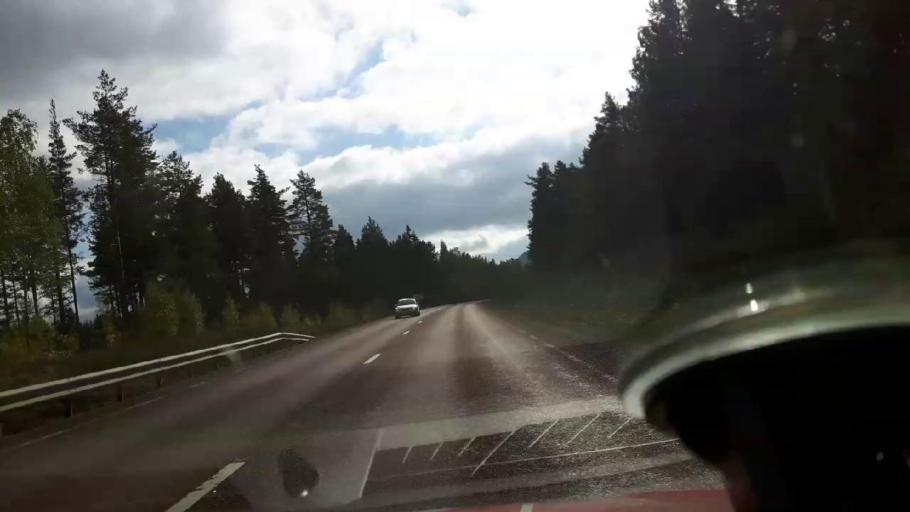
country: SE
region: Gaevleborg
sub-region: Bollnas Kommun
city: Arbra
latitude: 61.5857
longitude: 16.3135
